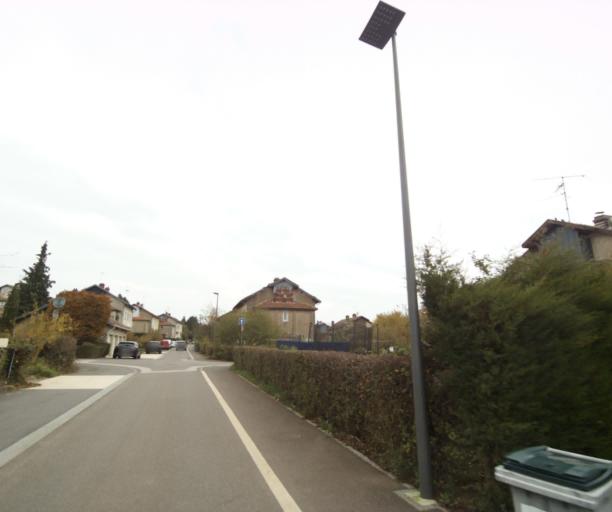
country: FR
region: Lorraine
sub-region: Departement de Meurthe-et-Moselle
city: Mancieulles
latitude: 49.2863
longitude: 5.8985
